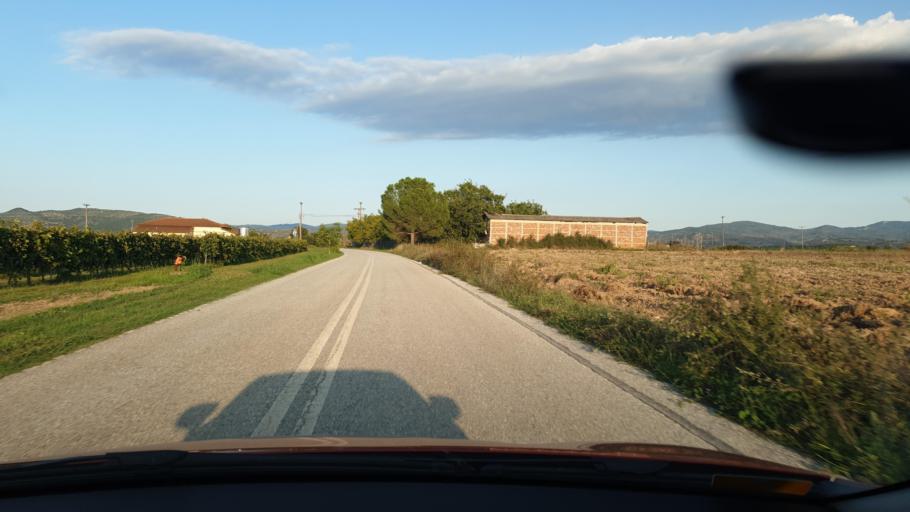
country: GR
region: Central Macedonia
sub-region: Nomos Thessalonikis
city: Nea Apollonia
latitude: 40.5557
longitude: 23.4631
